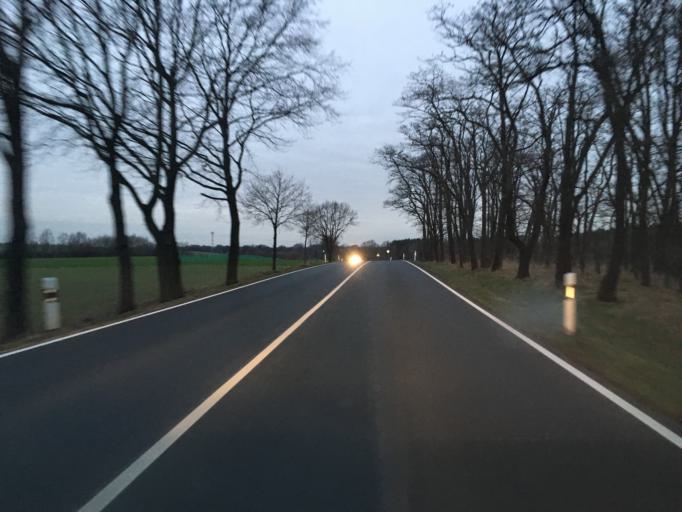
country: DE
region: Saxony
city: Dahlen
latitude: 51.3245
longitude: 13.0375
